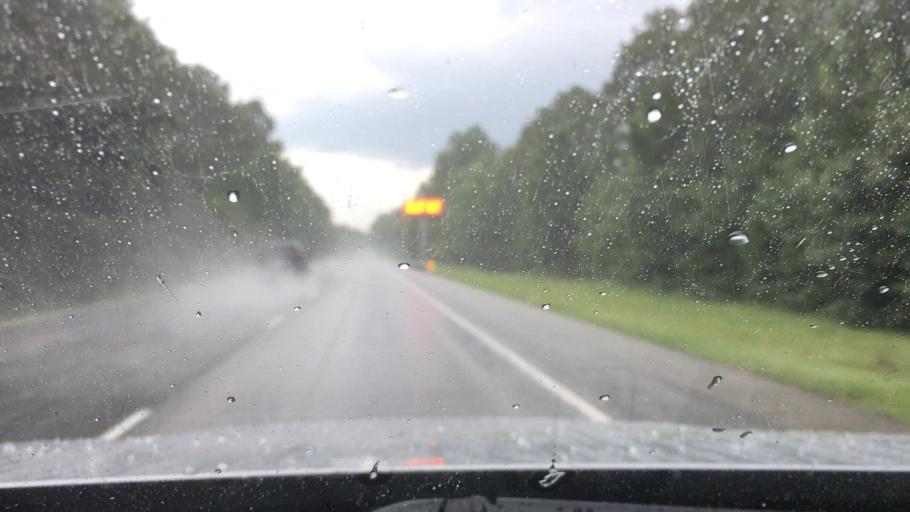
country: US
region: North Carolina
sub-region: Northampton County
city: Gaston
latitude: 36.4832
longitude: -77.6044
